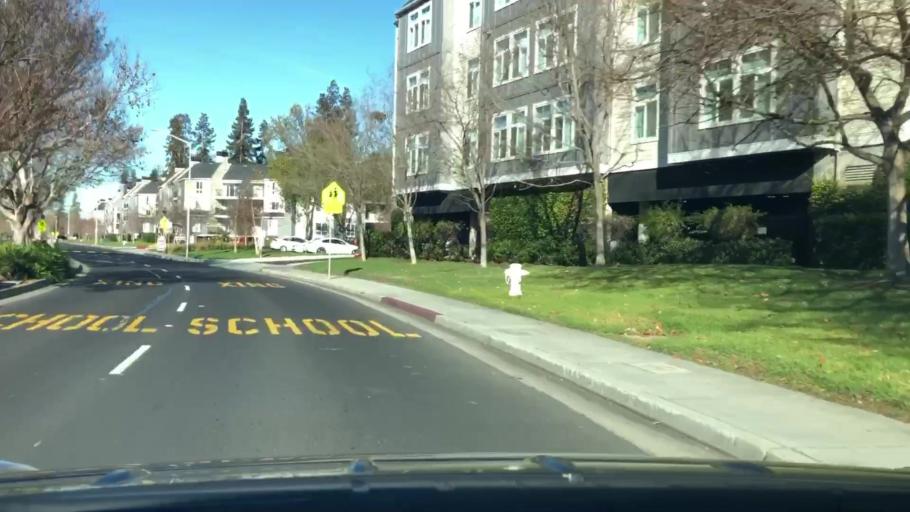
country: US
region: California
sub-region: Santa Clara County
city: Santa Clara
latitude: 37.3977
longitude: -121.9441
